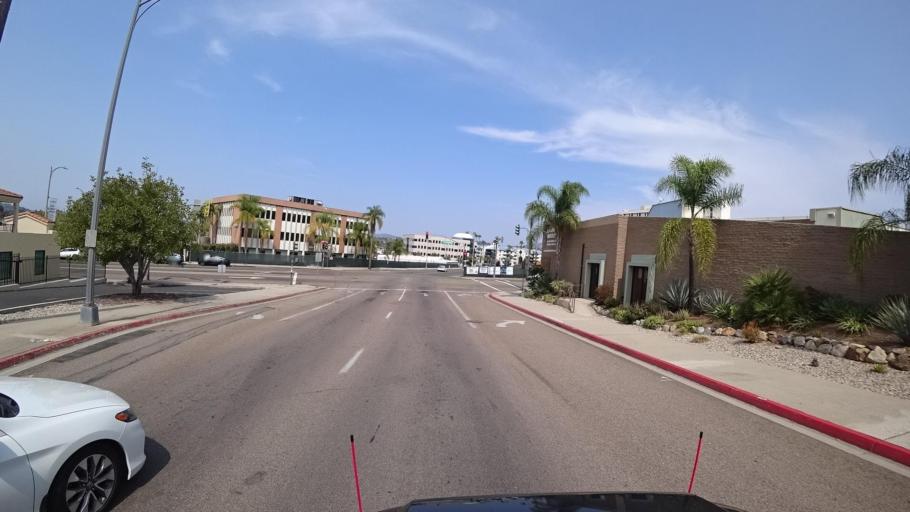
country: US
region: California
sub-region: San Diego County
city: Escondido
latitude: 33.1236
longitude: -117.0765
